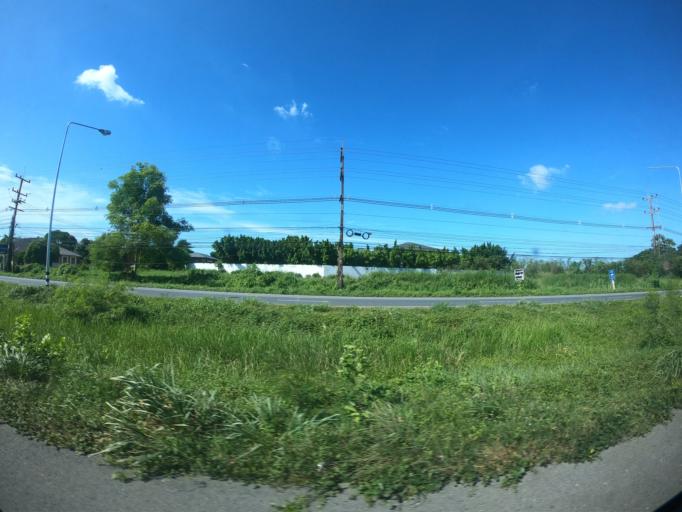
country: TH
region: Nakhon Nayok
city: Ban Na
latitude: 14.2543
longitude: 101.0904
